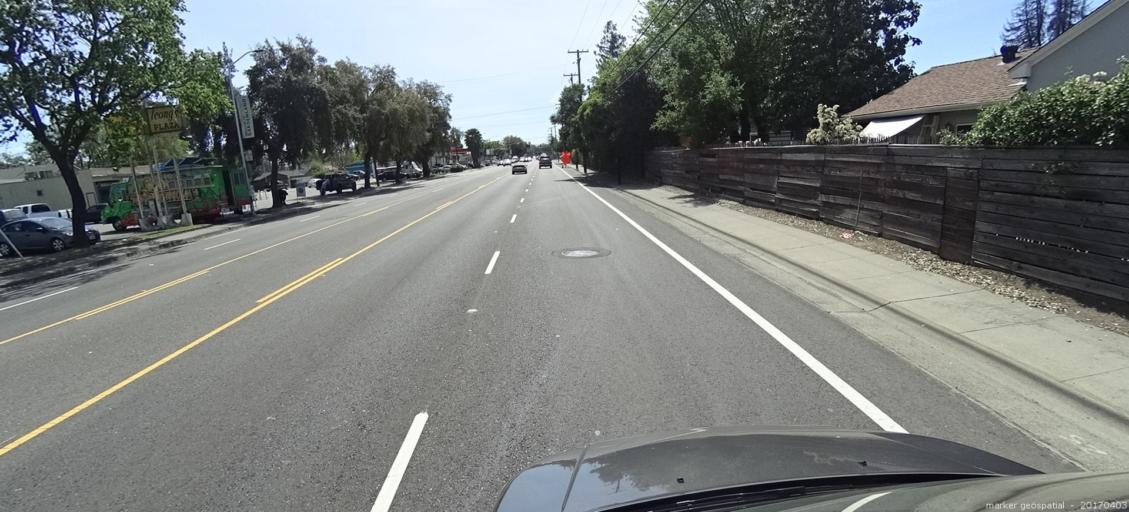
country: US
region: California
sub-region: Sacramento County
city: Sacramento
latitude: 38.6132
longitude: -121.4756
